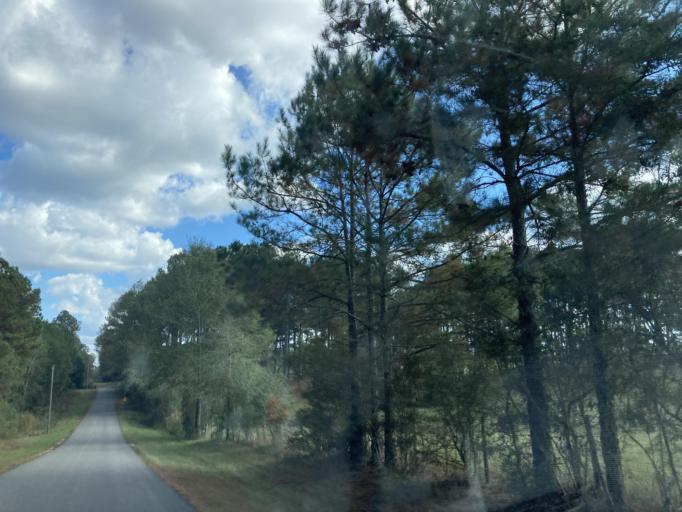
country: US
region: Mississippi
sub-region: Lamar County
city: Sumrall
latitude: 31.3756
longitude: -89.5489
